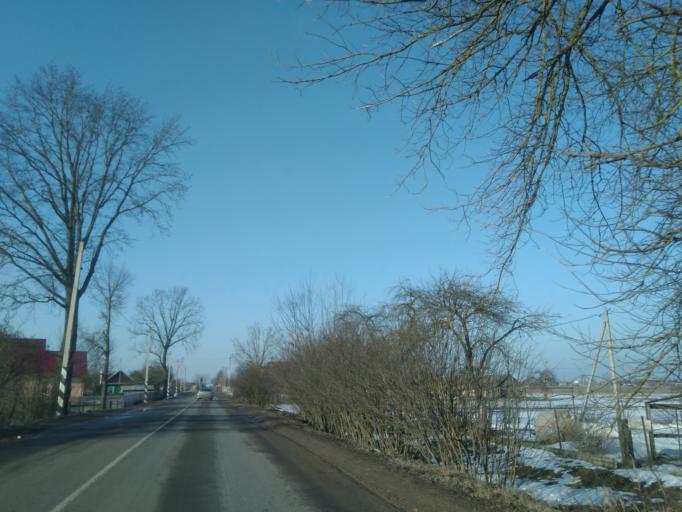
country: BY
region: Minsk
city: Snow
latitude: 53.2371
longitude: 26.3833
